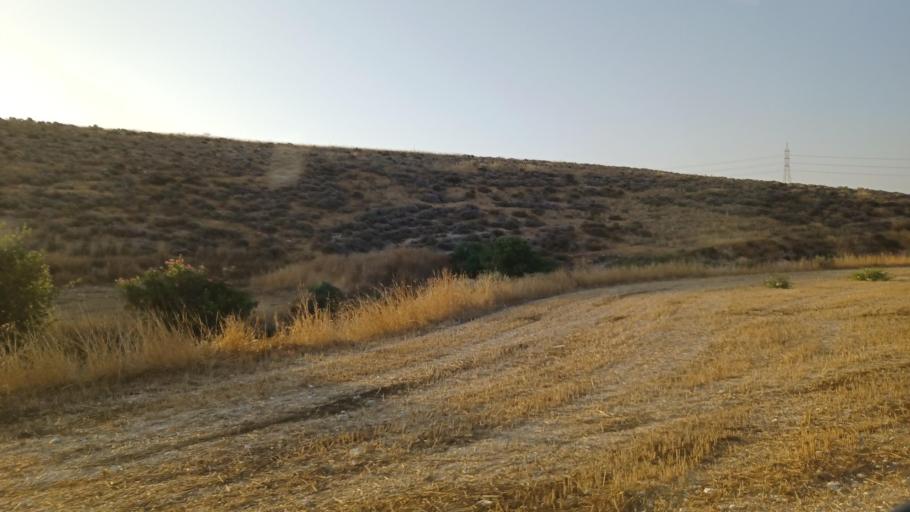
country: CY
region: Larnaka
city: Athienou
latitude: 34.9958
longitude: 33.5339
